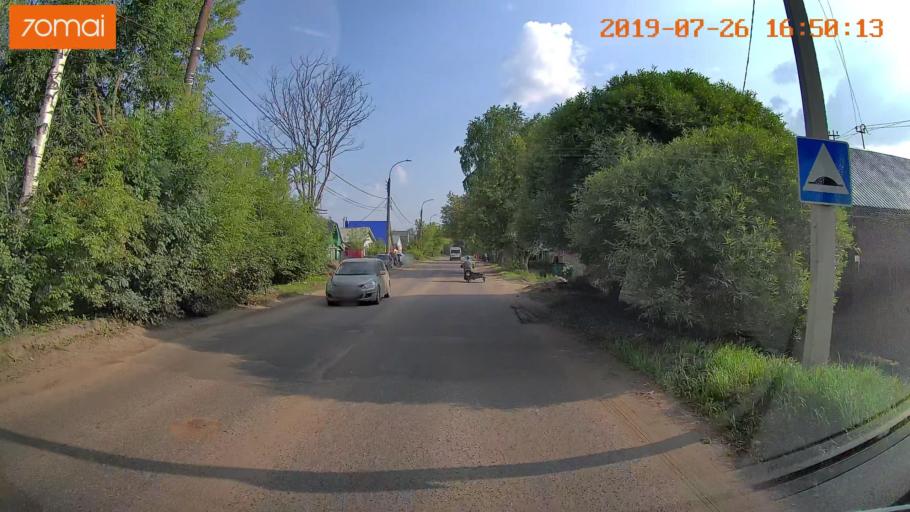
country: RU
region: Ivanovo
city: Bogorodskoye
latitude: 57.0253
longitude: 41.0207
